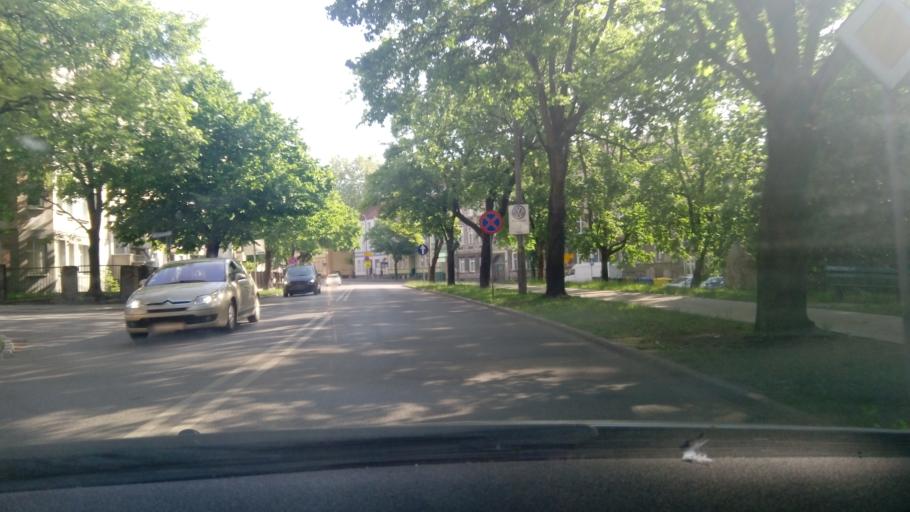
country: PL
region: Lubusz
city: Gorzow Wielkopolski
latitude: 52.7315
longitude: 15.2303
